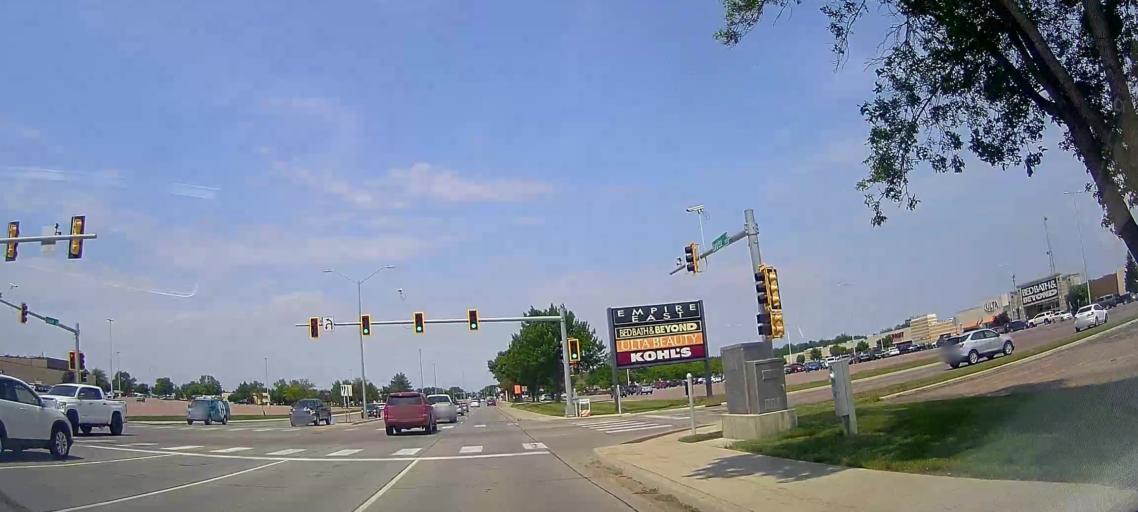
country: US
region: South Dakota
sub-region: Minnehaha County
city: Sioux Falls
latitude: 43.5099
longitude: -96.7711
